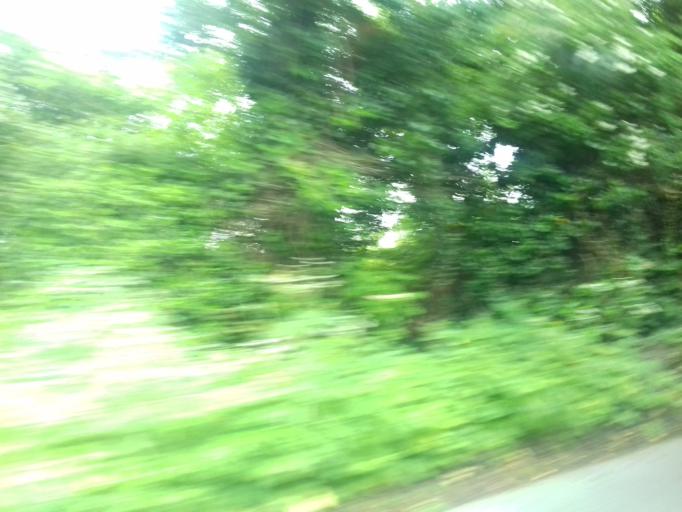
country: IE
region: Leinster
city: Donabate
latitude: 53.4937
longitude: -6.1886
